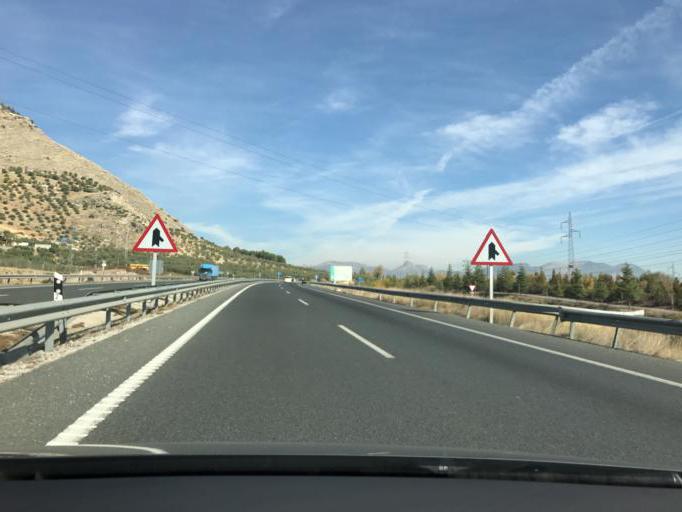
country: ES
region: Andalusia
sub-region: Provincia de Granada
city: Atarfe
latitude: 37.2297
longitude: -3.6907
